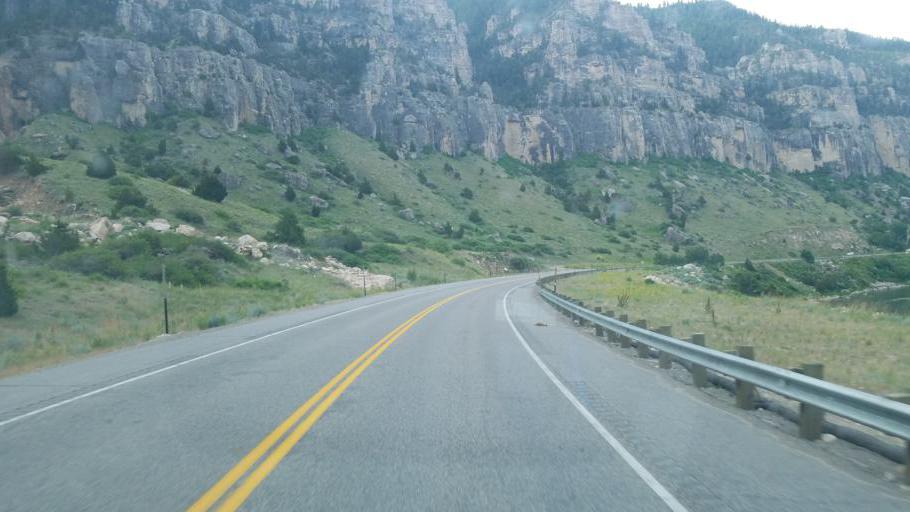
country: US
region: Wyoming
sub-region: Hot Springs County
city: Thermopolis
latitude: 43.5275
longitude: -108.1755
